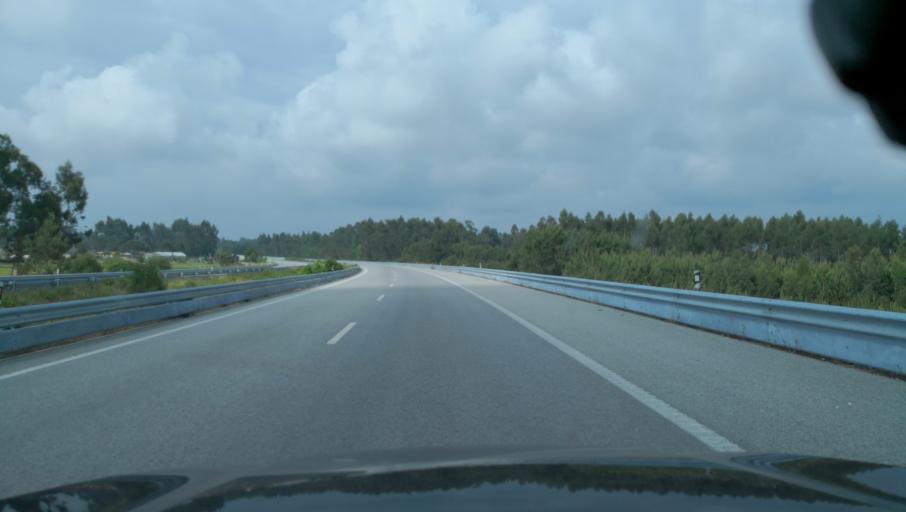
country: PT
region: Coimbra
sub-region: Montemor-O-Velho
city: Arazede
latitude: 40.3028
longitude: -8.7368
